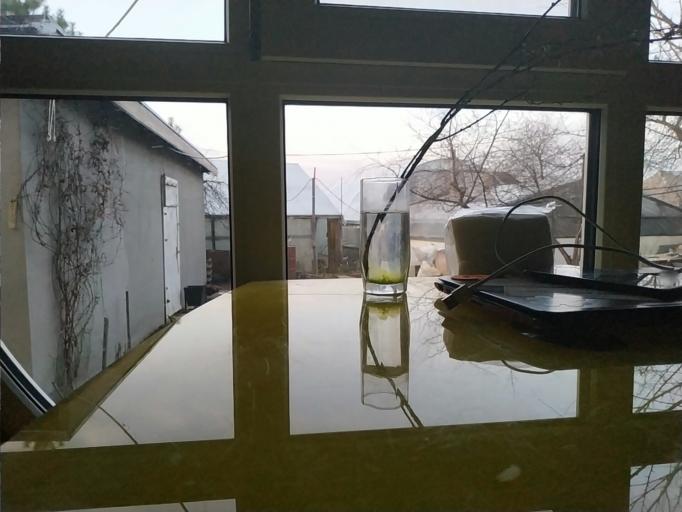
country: RU
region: Republic of Karelia
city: Suoyarvi
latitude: 62.5595
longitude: 31.9540
